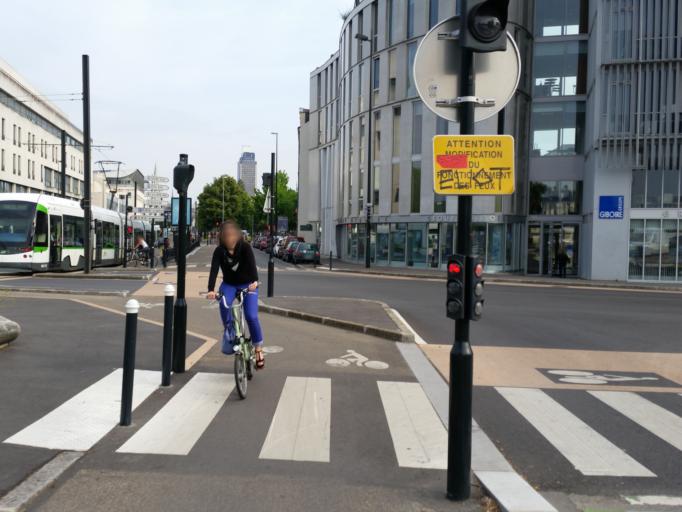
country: FR
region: Pays de la Loire
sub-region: Departement de la Loire-Atlantique
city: Nantes
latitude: 47.2086
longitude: -1.5496
